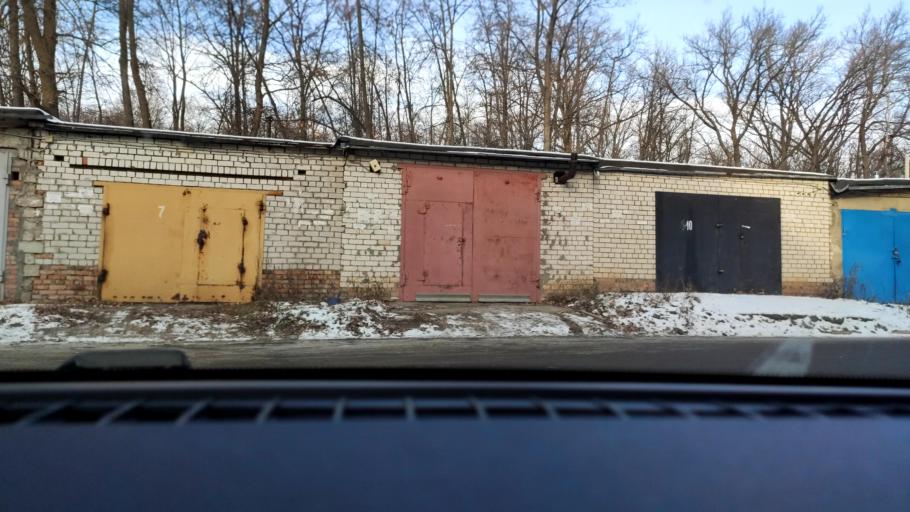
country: RU
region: Samara
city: Petra-Dubrava
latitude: 53.3033
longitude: 50.2670
